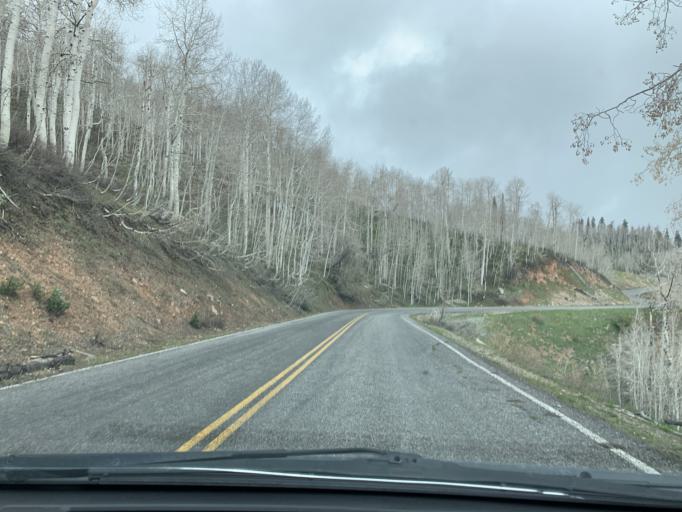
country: US
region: Utah
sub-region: Utah County
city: Elk Ridge
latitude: 39.8801
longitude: -111.6866
